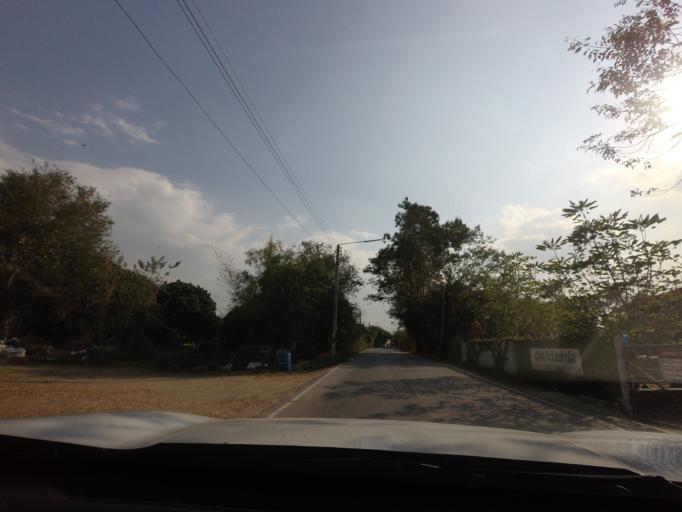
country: TH
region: Nakhon Ratchasima
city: Pak Chong
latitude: 14.6202
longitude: 101.4471
